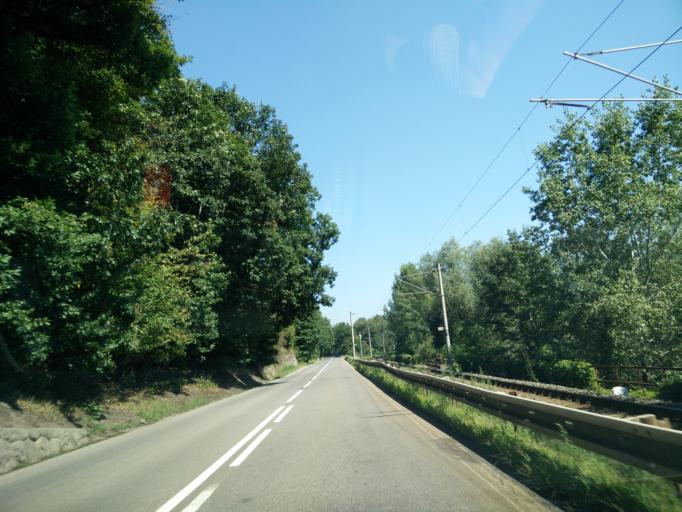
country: SK
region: Banskobystricky
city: Nova Bana
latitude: 48.3944
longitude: 18.6118
